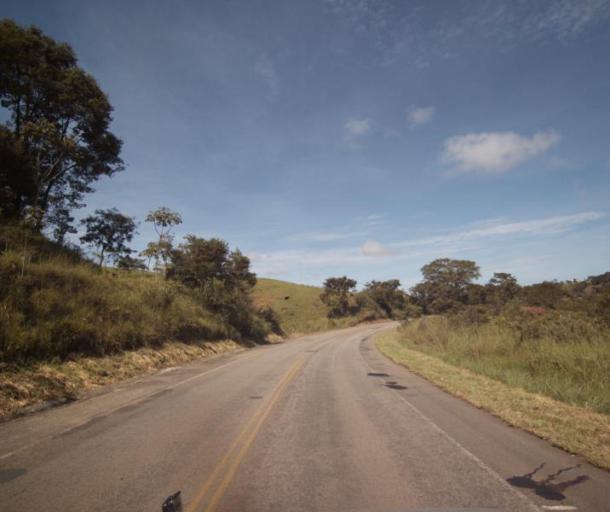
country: BR
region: Goias
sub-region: Abadiania
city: Abadiania
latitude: -16.1149
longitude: -48.8869
